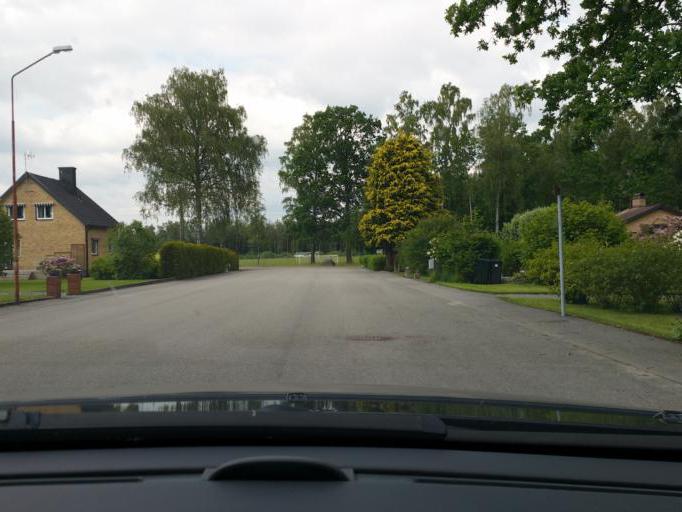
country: SE
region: Kronoberg
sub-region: Vaxjo Kommun
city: Lammhult
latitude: 57.1754
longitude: 14.5899
